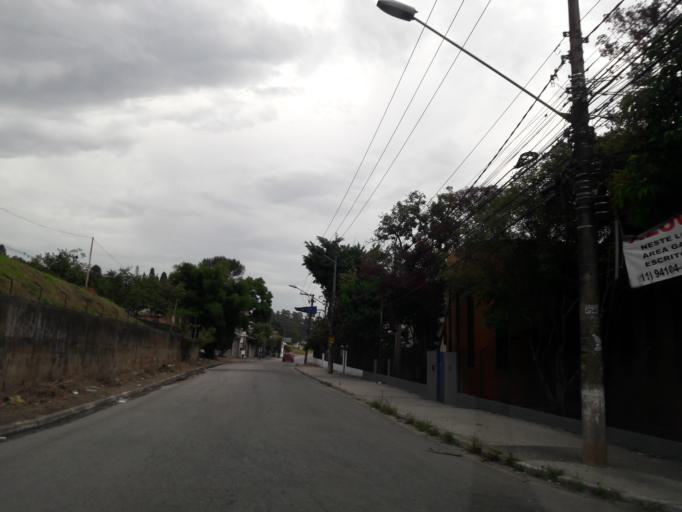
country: BR
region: Sao Paulo
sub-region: Itaquaquecetuba
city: Itaquaquecetuba
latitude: -23.4234
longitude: -46.4003
